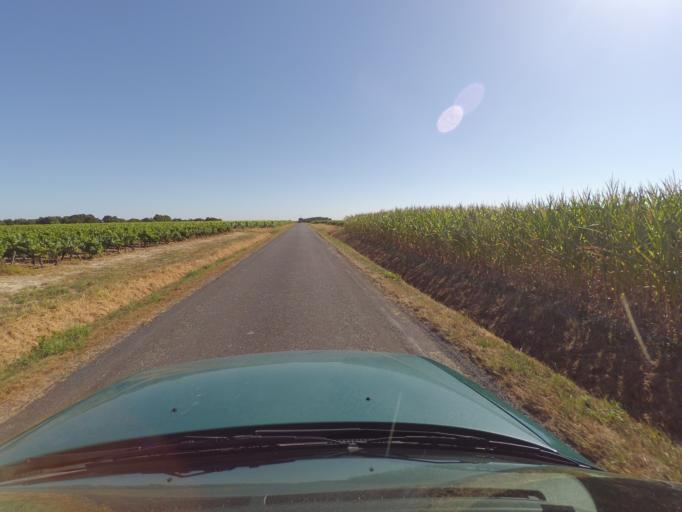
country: FR
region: Pays de la Loire
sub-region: Departement de la Loire-Atlantique
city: Maisdon-sur-Sevre
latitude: 47.0891
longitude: -1.3710
